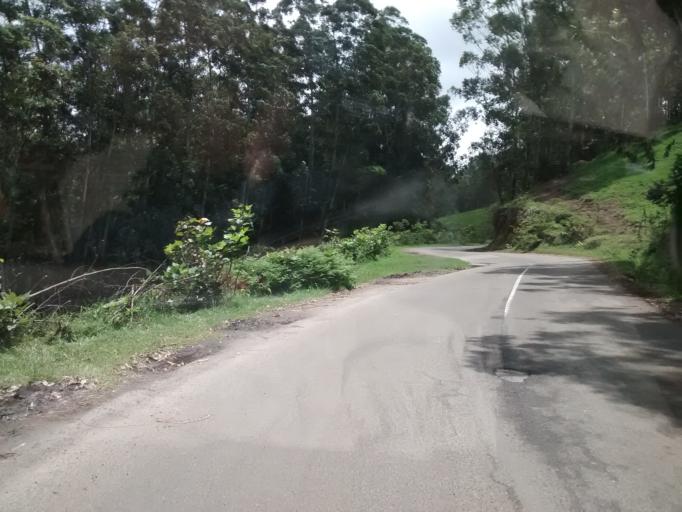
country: IN
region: Kerala
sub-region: Idukki
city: Munnar
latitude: 10.1134
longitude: 77.1334
